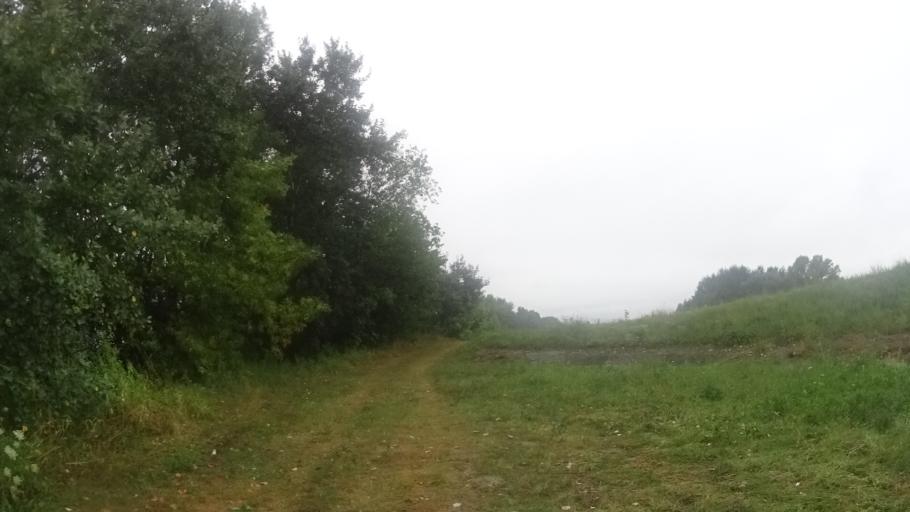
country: HU
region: Komarom-Esztergom
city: Nyergesujfalu
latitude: 47.7621
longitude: 18.5271
